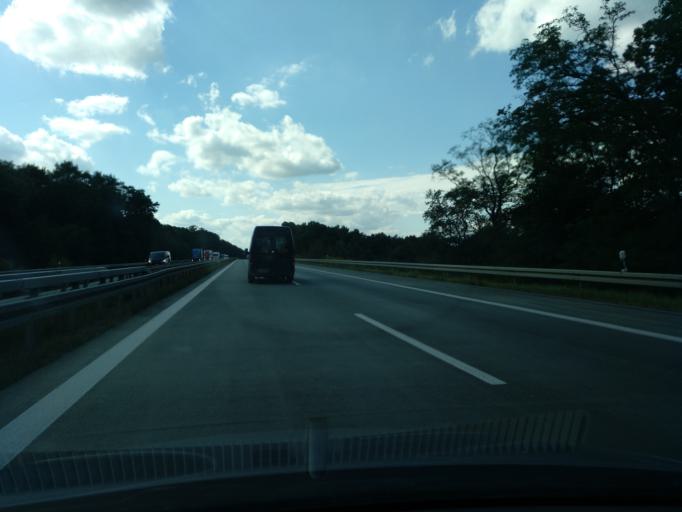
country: DE
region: Brandenburg
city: Rauen
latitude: 52.3294
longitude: 14.0380
